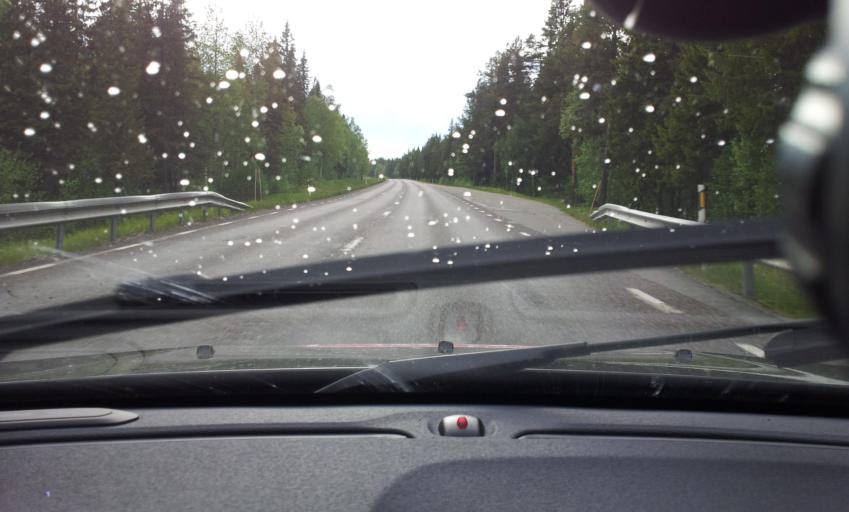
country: SE
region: Jaemtland
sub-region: OEstersunds Kommun
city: Brunflo
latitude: 63.2019
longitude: 14.9313
